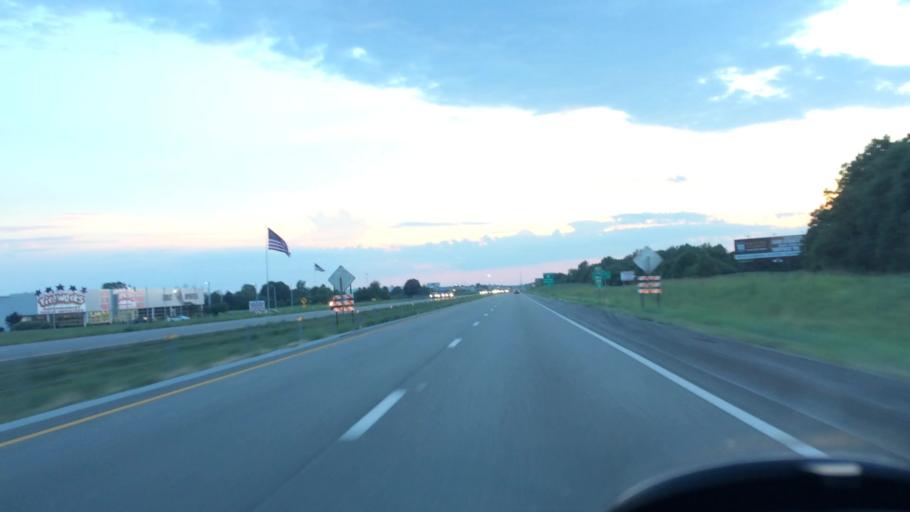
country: US
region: Missouri
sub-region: Greene County
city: Strafford
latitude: 37.2503
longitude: -93.1969
